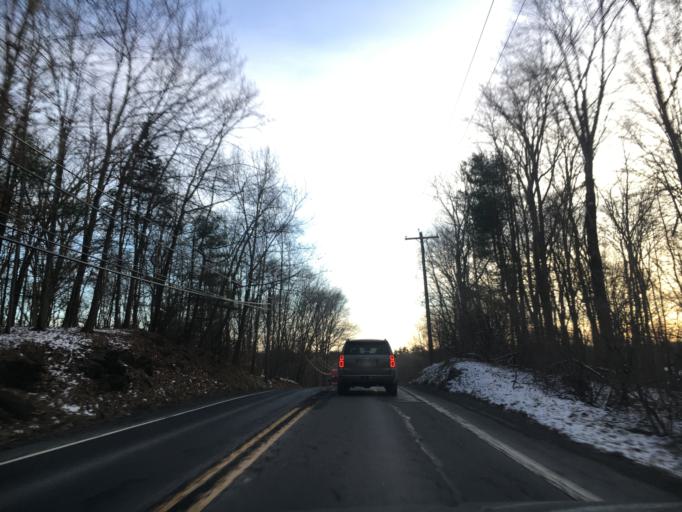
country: US
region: Pennsylvania
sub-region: Pike County
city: Saw Creek
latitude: 41.0667
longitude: -75.1149
